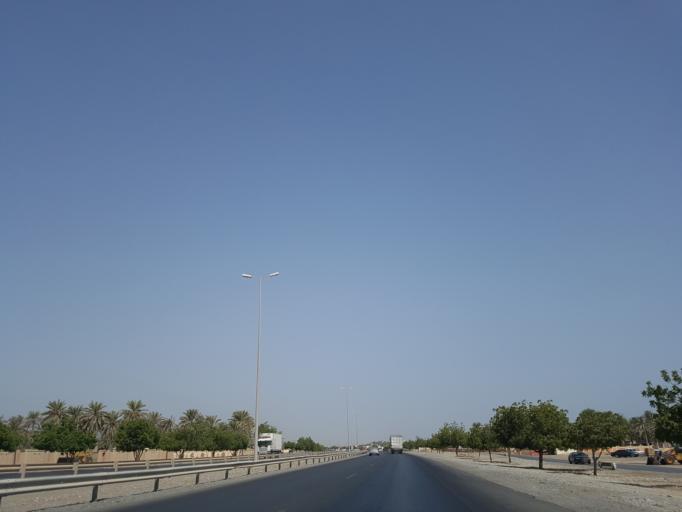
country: OM
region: Al Batinah
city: As Suwayq
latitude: 23.7488
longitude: 57.6157
